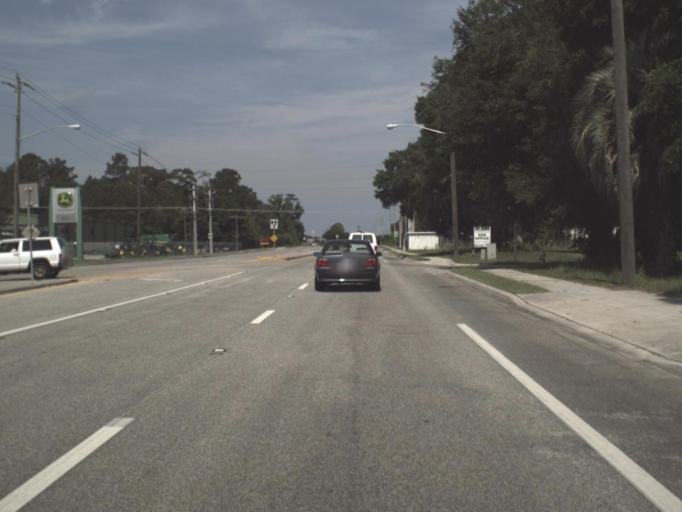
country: US
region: Florida
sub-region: Putnam County
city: East Palatka
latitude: 29.7144
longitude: -81.5118
